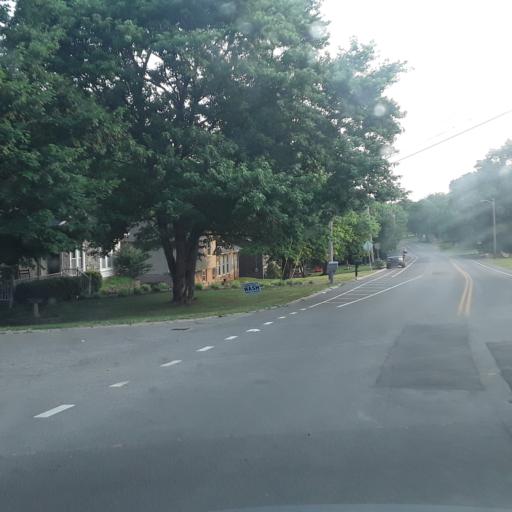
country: US
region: Tennessee
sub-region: Williamson County
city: Brentwood Estates
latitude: 36.0499
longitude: -86.7244
